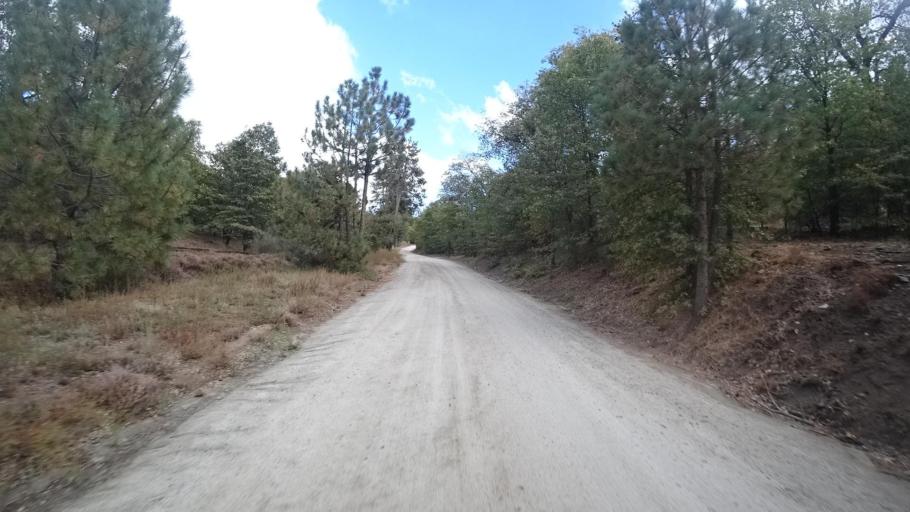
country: US
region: California
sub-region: San Diego County
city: Pine Valley
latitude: 32.8688
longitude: -116.4228
